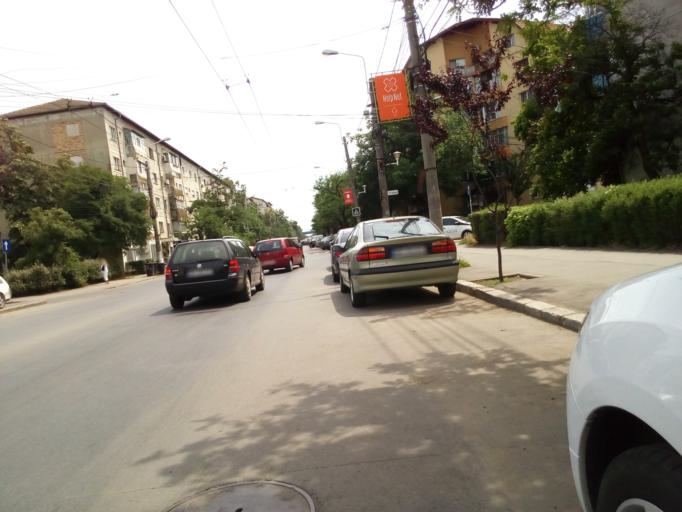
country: RO
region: Timis
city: Timisoara
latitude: 45.7375
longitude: 21.2381
